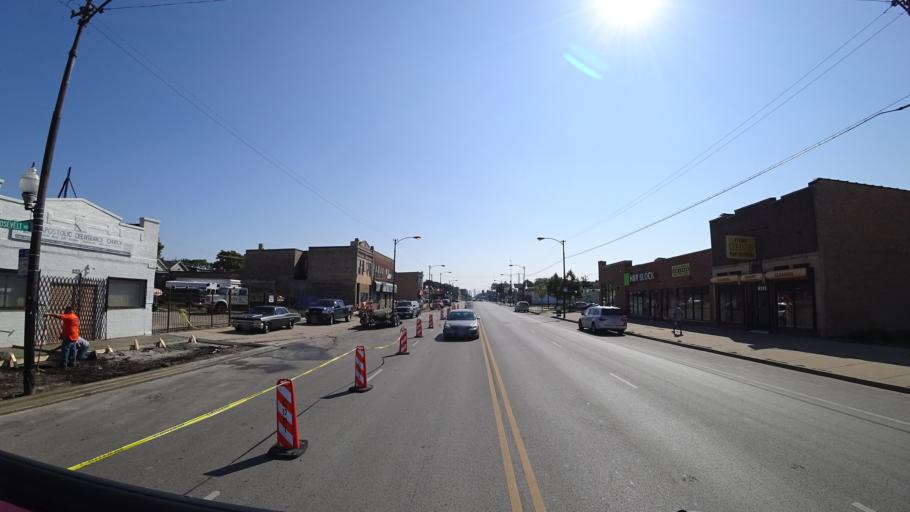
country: US
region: Illinois
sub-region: Cook County
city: Cicero
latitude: 41.8662
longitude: -87.7226
